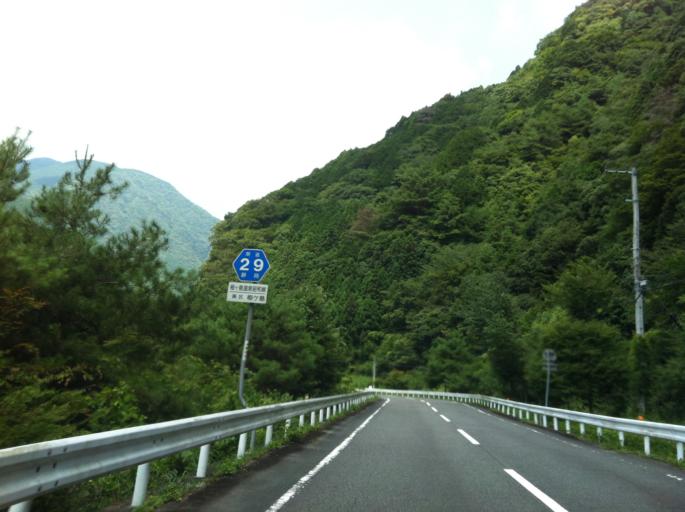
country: JP
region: Shizuoka
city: Shizuoka-shi
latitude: 35.2524
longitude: 138.3391
